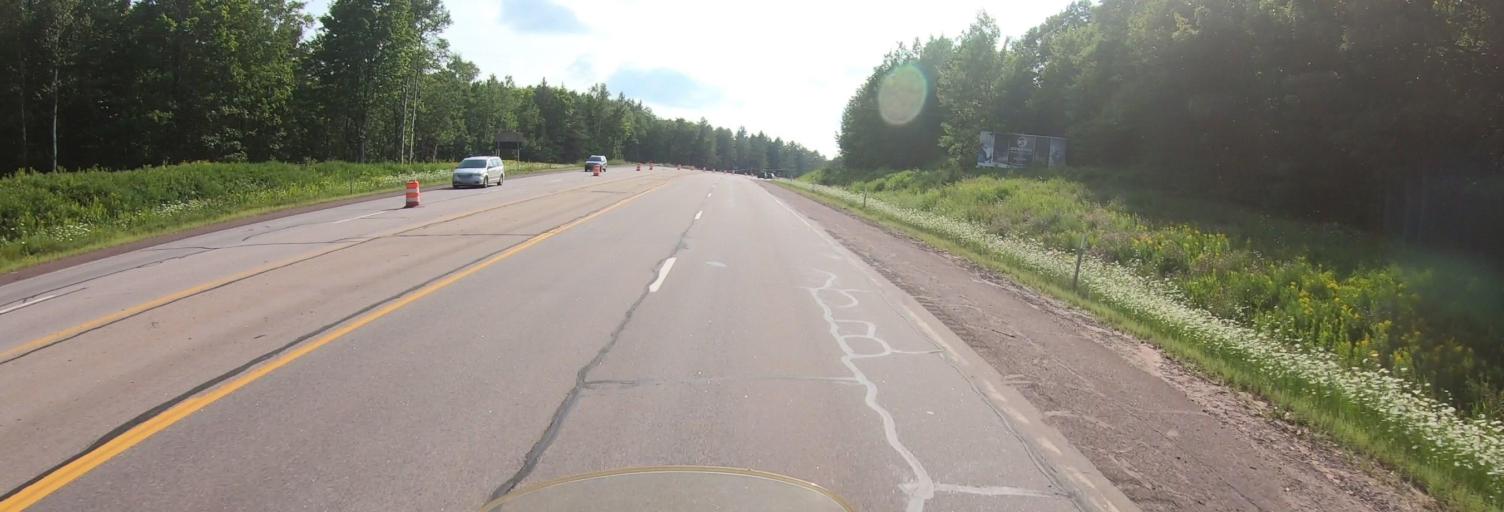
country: US
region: Michigan
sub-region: Gogebic County
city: Bessemer
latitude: 46.4800
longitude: -90.0873
